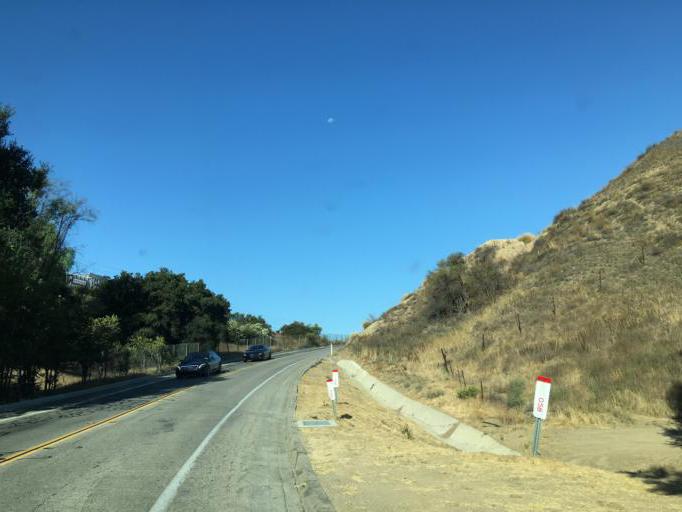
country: US
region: California
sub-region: Los Angeles County
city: Hidden Hills
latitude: 34.1500
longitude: -118.6732
